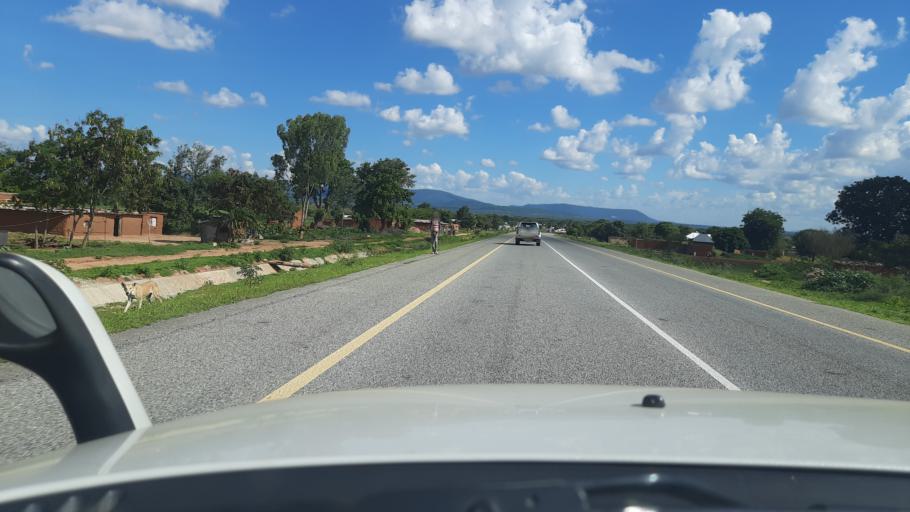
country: TZ
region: Dodoma
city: Kondoa
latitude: -5.1038
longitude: 35.8211
